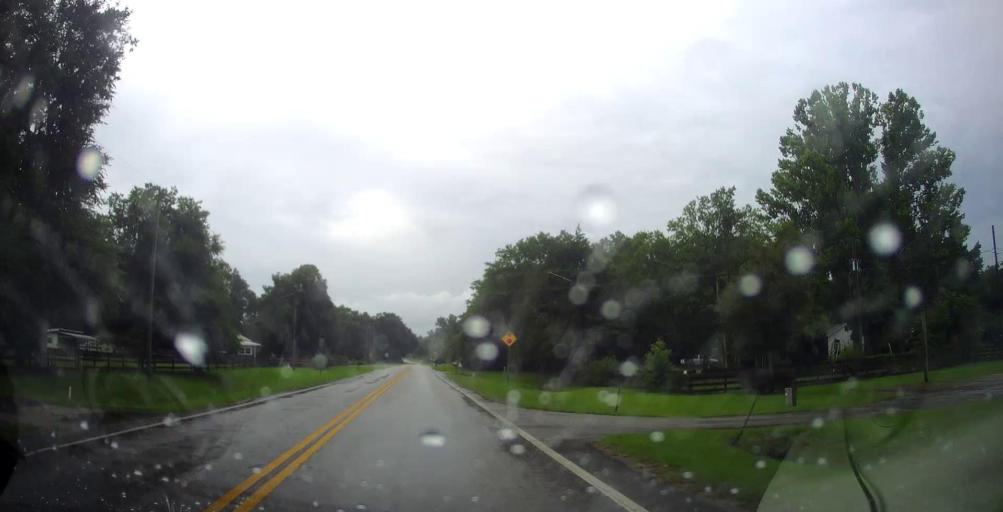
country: US
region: Florida
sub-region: Marion County
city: Citra
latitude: 29.3685
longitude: -82.2512
